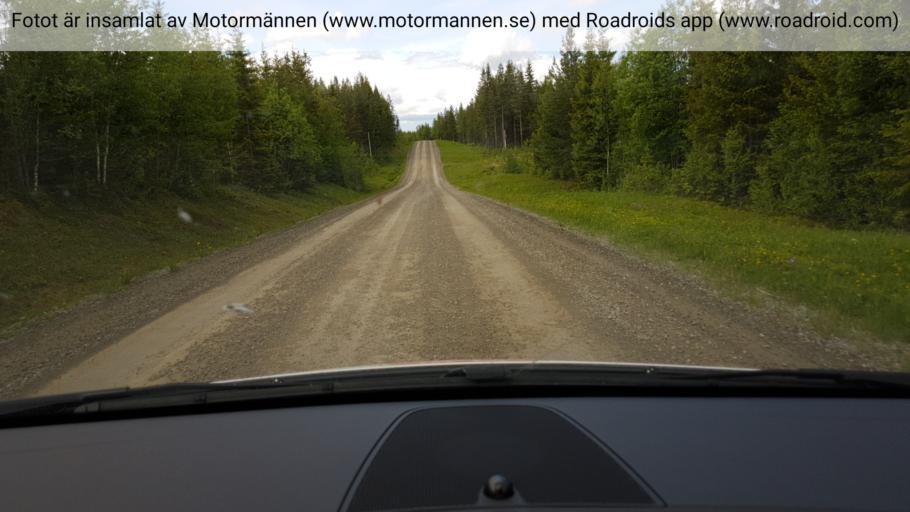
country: SE
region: Jaemtland
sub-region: Bergs Kommun
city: Hoverberg
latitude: 62.9955
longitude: 14.1551
